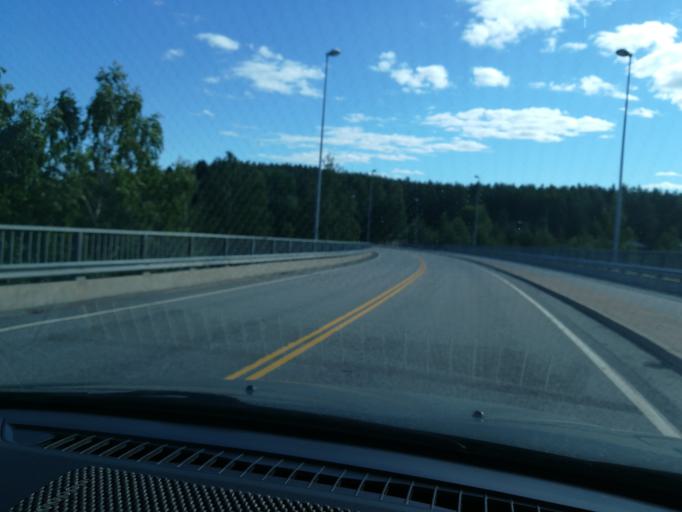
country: FI
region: Southern Savonia
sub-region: Mikkeli
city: Puumala
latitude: 61.5175
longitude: 28.1734
